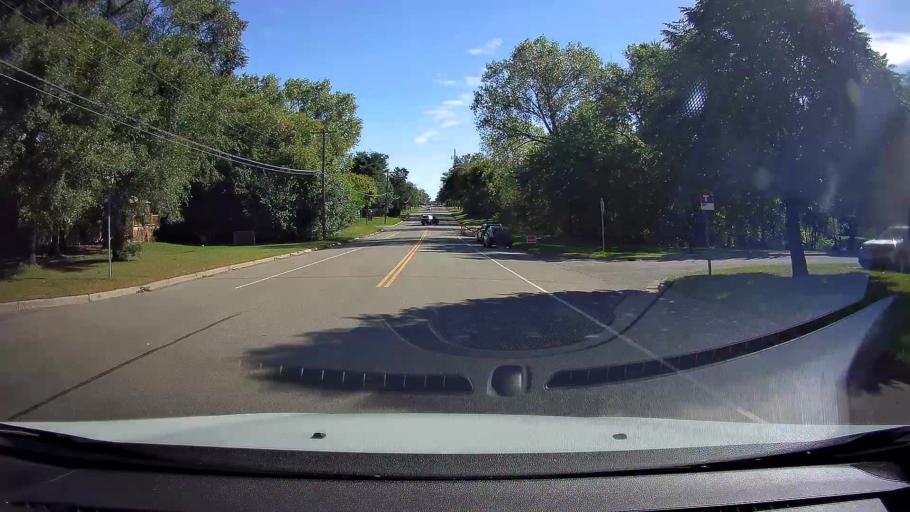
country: US
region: Minnesota
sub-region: Ramsey County
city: Roseville
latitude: 45.0228
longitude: -93.1529
